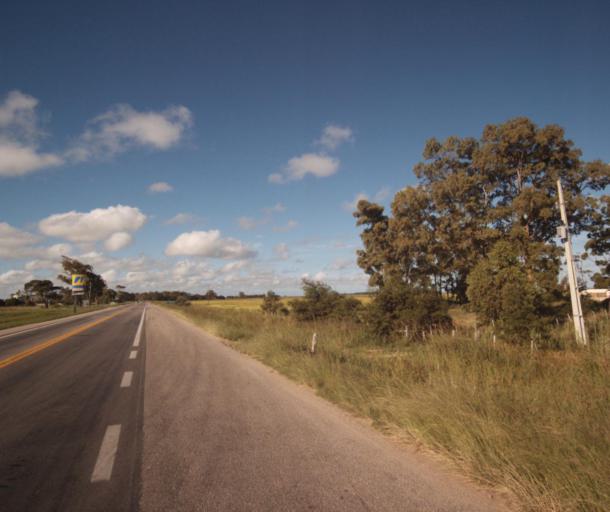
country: BR
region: Rio Grande do Sul
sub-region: Arroio Grande
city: Arroio Grande
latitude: -32.8537
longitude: -52.7038
